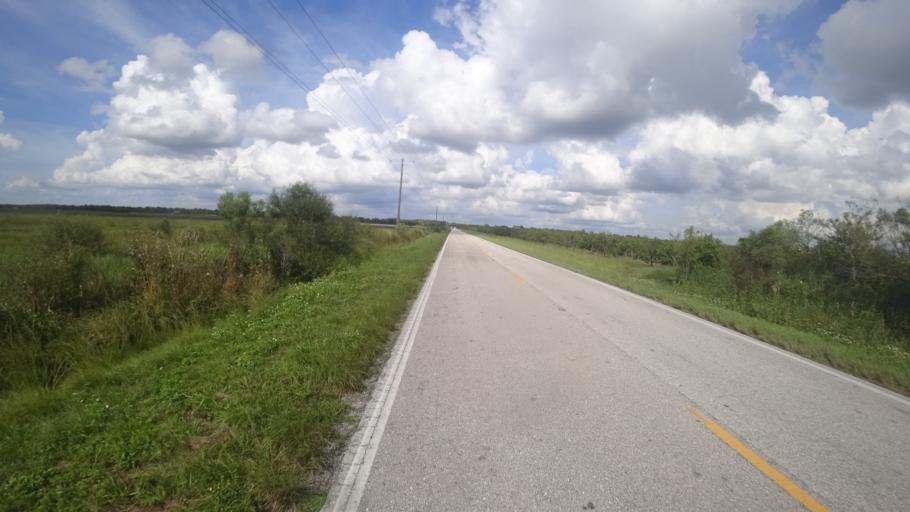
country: US
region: Florida
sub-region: Hillsborough County
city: Wimauma
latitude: 27.5821
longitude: -82.1041
